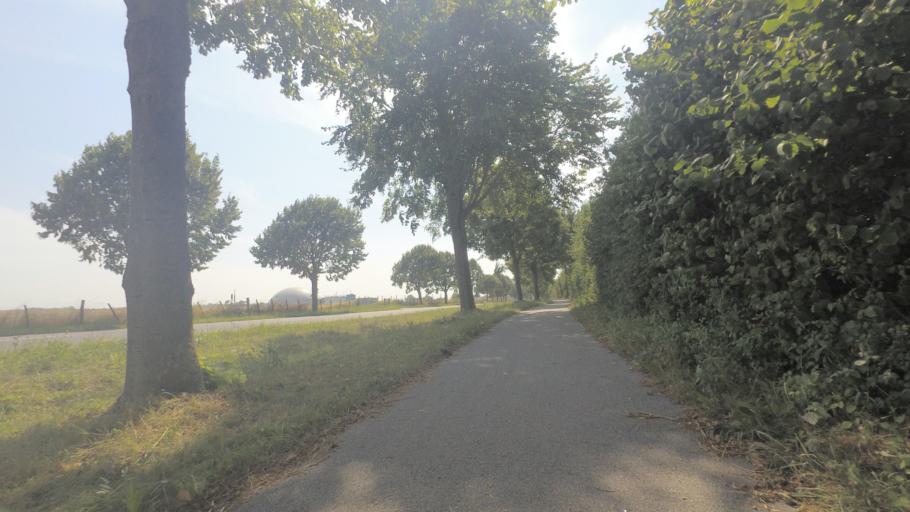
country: DE
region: Mecklenburg-Vorpommern
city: Poseritz
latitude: 54.2294
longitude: 13.2742
